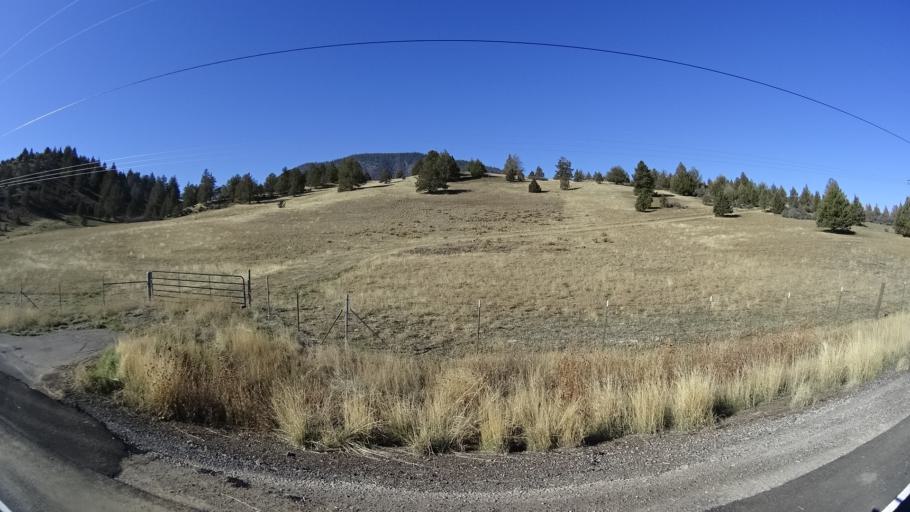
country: US
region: California
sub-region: Siskiyou County
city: Montague
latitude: 41.8644
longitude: -122.4641
